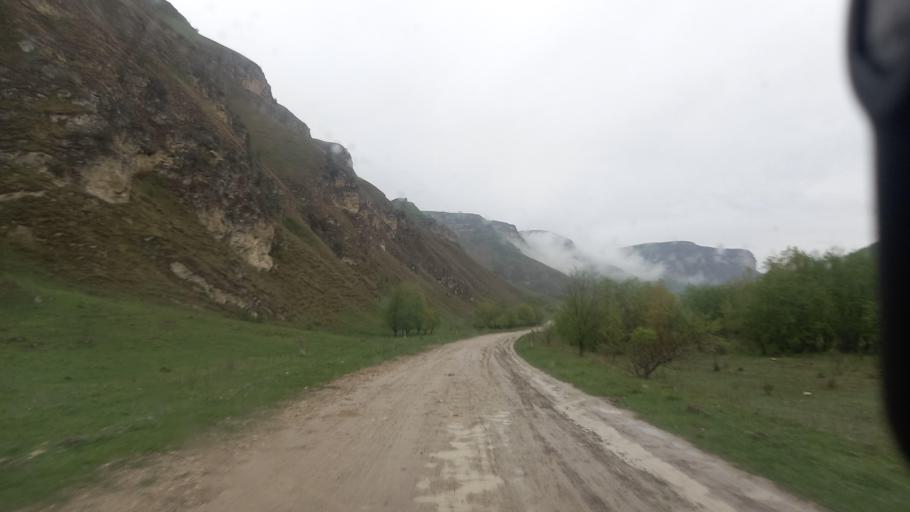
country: RU
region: Kabardino-Balkariya
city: Gundelen
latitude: 43.5985
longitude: 43.0578
